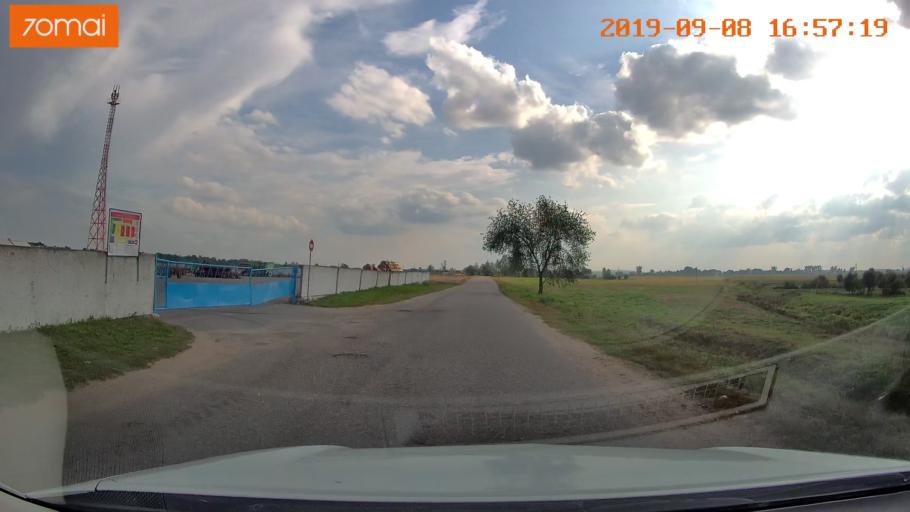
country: BY
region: Grodnenskaya
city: Hrodna
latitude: 53.7338
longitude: 23.9283
